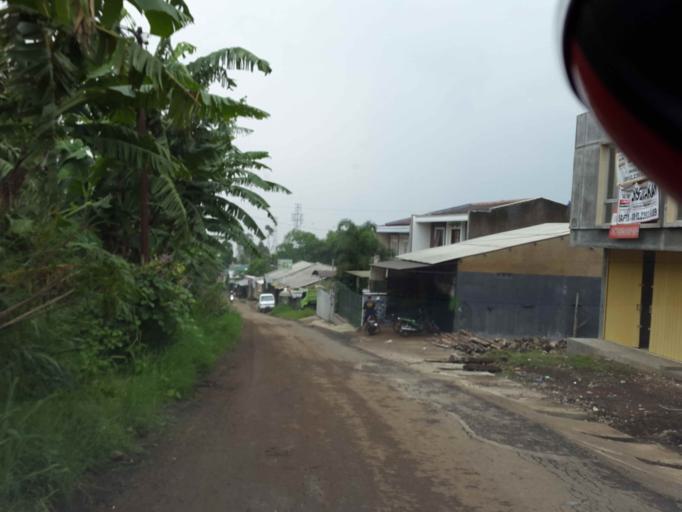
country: ID
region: West Java
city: Cimahi
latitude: -6.8462
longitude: 107.5824
